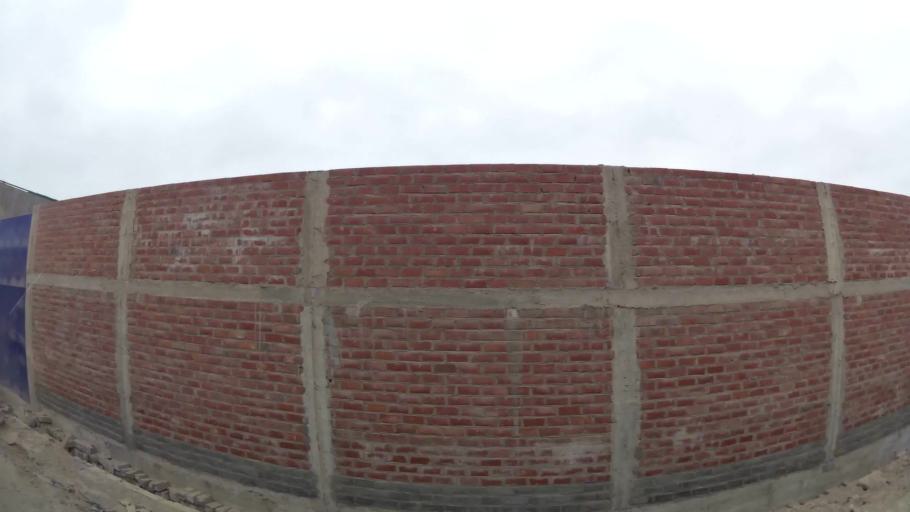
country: PE
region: Lima
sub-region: Lima
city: Surco
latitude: -12.2009
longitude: -76.9711
